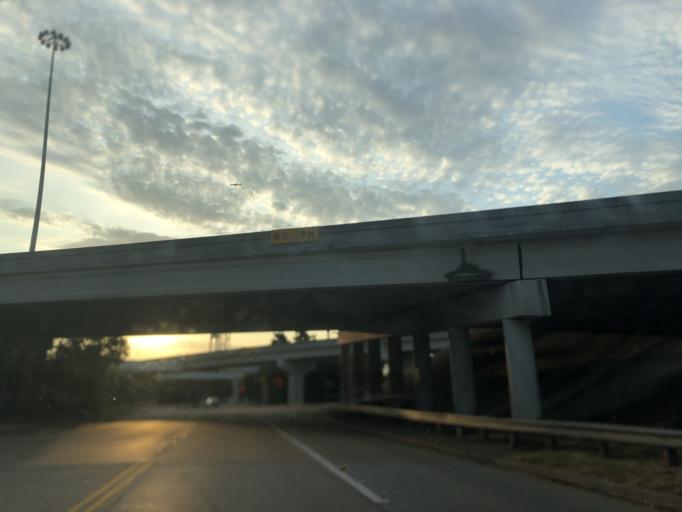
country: US
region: Texas
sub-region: Tarrant County
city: Arlington
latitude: 32.7580
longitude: -97.0769
